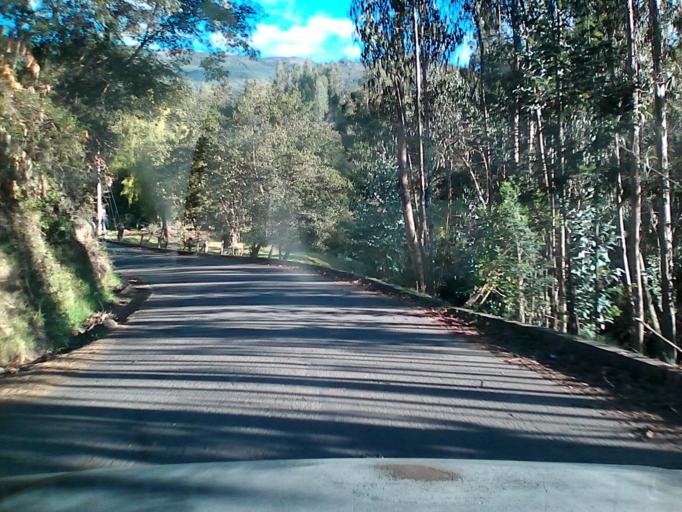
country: CO
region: Boyaca
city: Duitama
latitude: 5.8647
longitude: -73.0278
